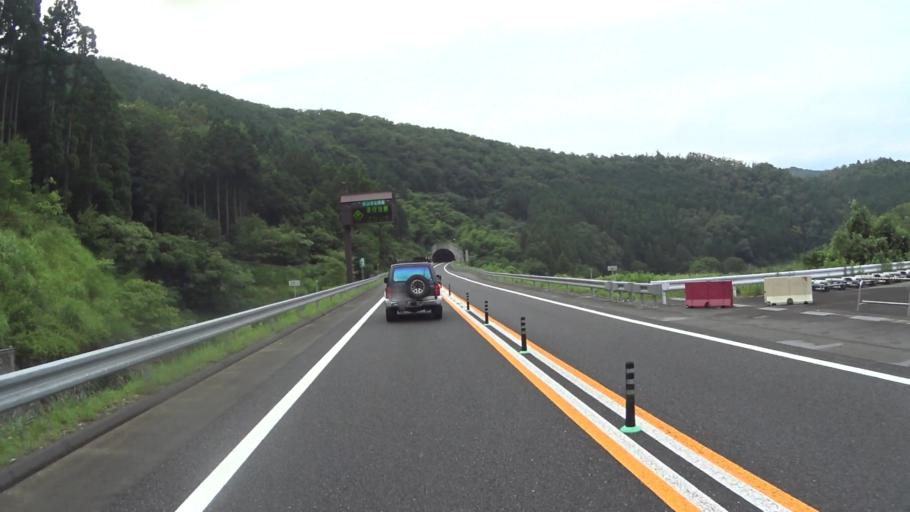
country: JP
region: Kyoto
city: Ayabe
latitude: 35.3133
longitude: 135.3221
